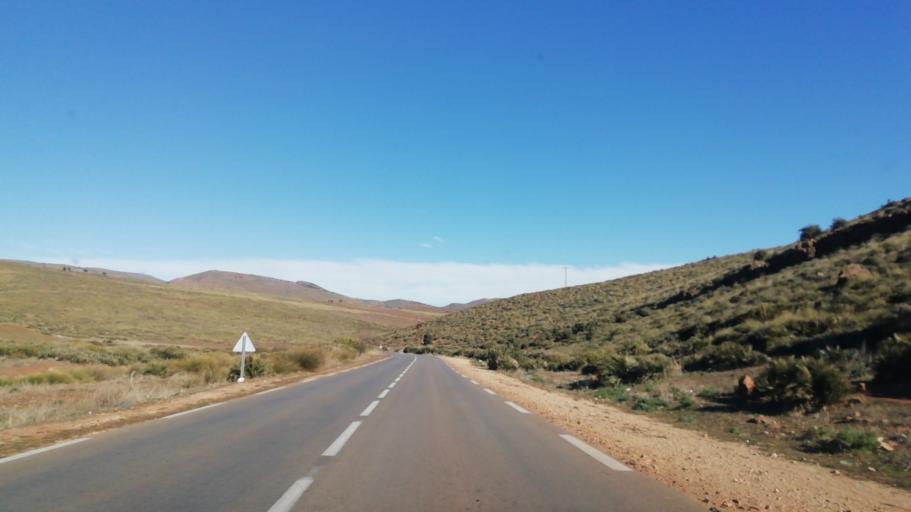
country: DZ
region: Tlemcen
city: Ouled Mimoun
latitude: 34.7682
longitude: -1.1366
